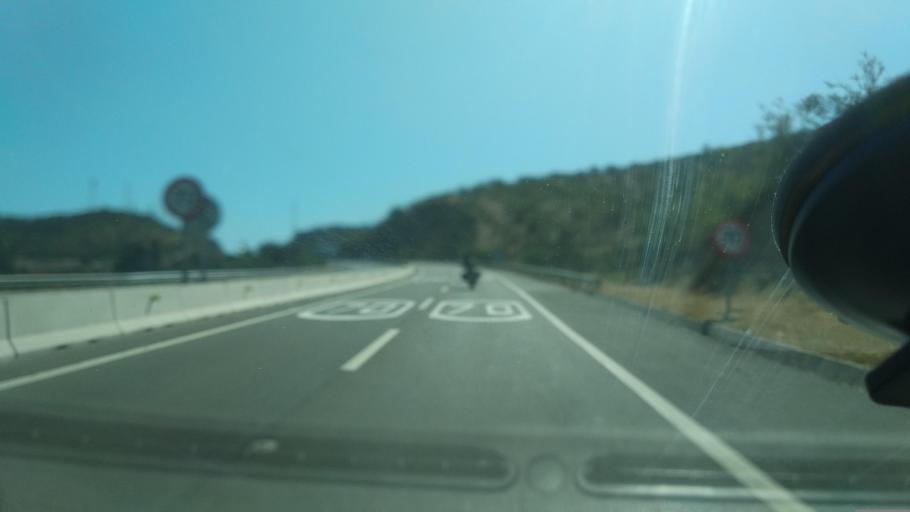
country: CL
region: Valparaiso
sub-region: Provincia de Marga Marga
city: Villa Alemana
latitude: -33.0440
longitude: -71.3216
